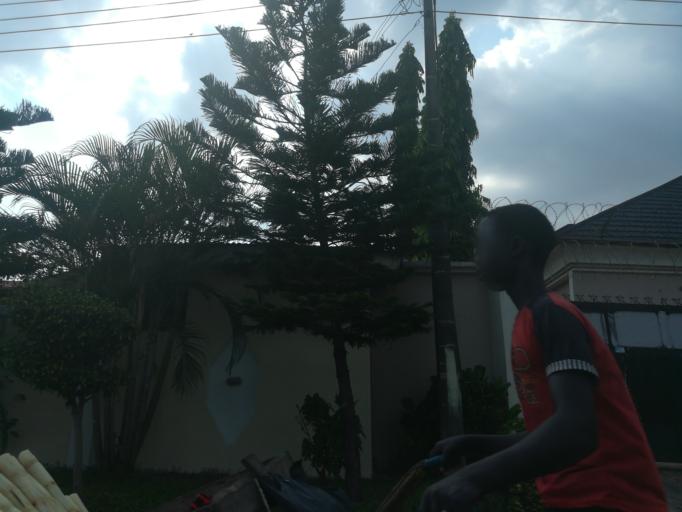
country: NG
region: Abuja Federal Capital Territory
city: Abuja
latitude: 9.0794
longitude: 7.4155
